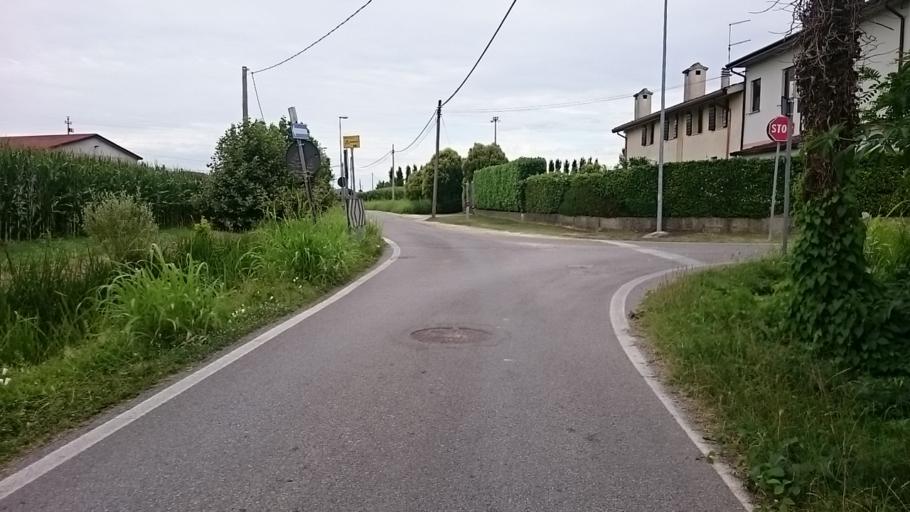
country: IT
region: Veneto
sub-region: Provincia di Padova
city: Masera di Padova
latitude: 45.3339
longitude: 11.8758
